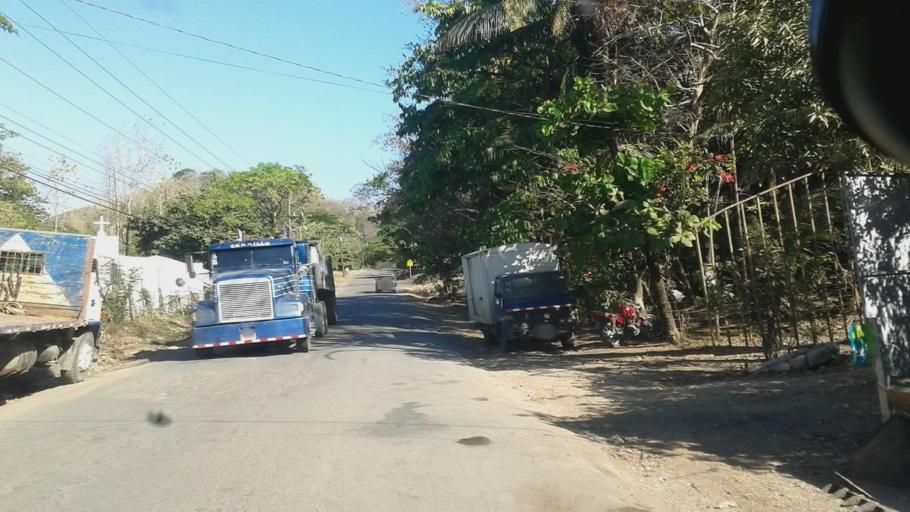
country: CR
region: Guanacaste
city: Samara
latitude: 9.9029
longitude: -85.5904
